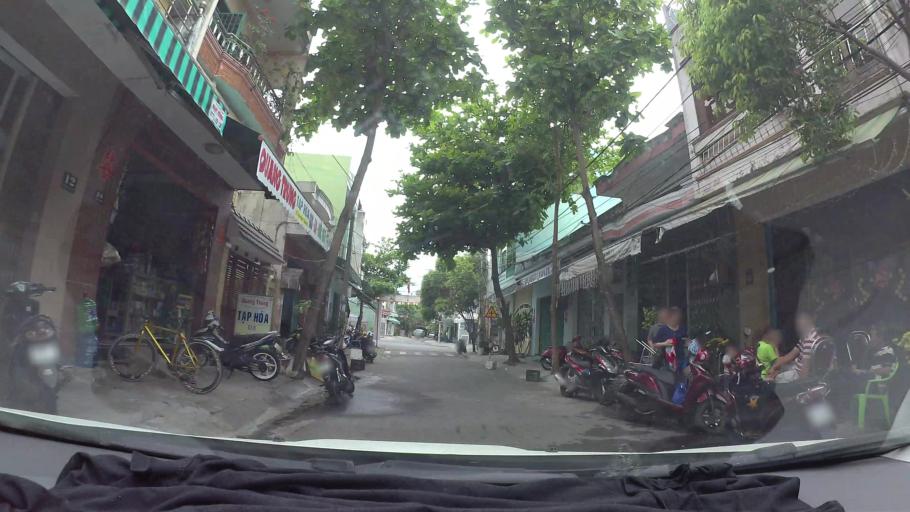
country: VN
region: Da Nang
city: Thanh Khe
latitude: 16.0751
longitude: 108.1764
